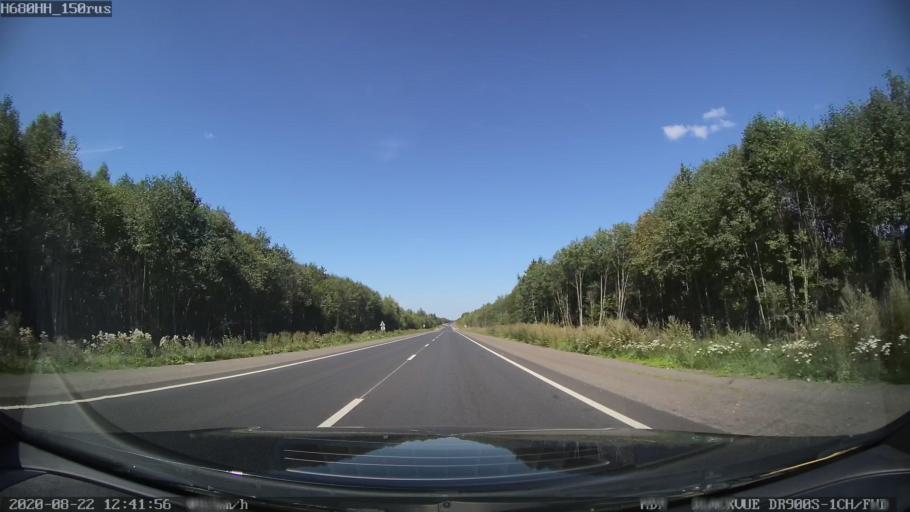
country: RU
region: Tverskaya
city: Rameshki
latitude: 57.3543
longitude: 36.0980
